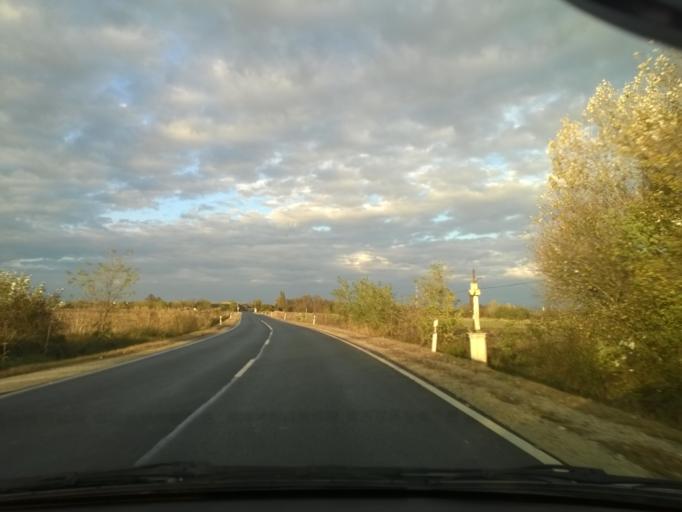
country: HU
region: Bacs-Kiskun
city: Dunapataj
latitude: 46.6297
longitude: 18.9993
